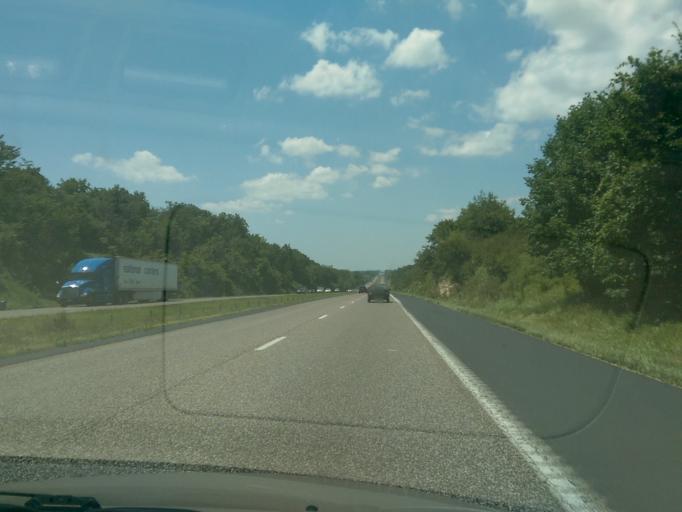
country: US
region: Missouri
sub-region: Cooper County
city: Boonville
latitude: 38.9396
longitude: -92.6066
